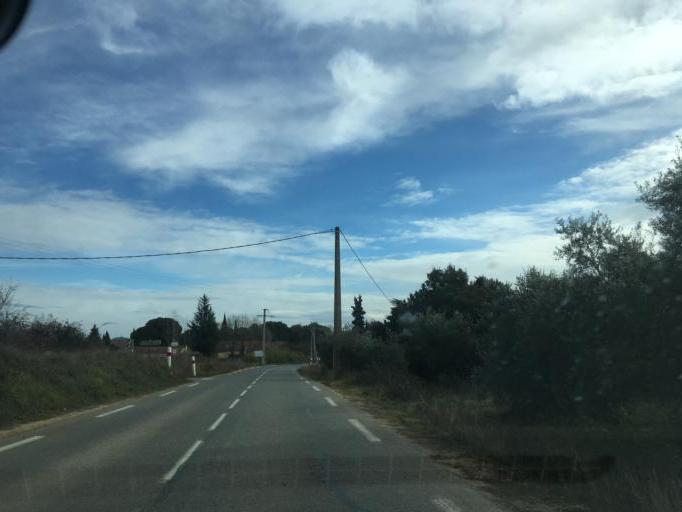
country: FR
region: Provence-Alpes-Cote d'Azur
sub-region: Departement du Var
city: Le Val
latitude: 43.4405
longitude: 6.0559
